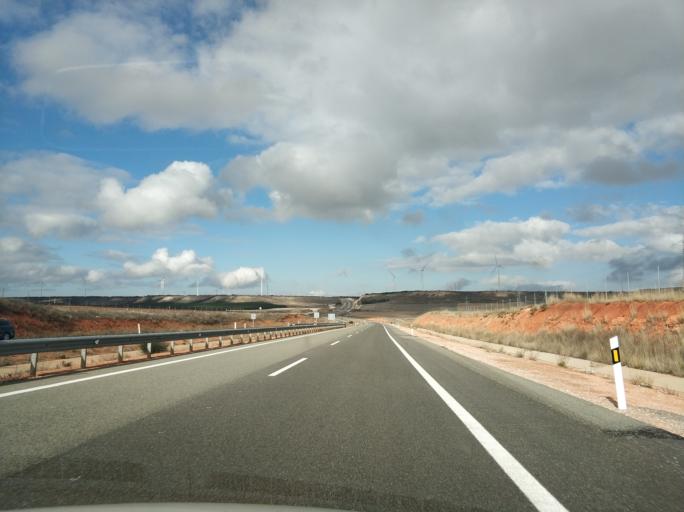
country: ES
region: Castille and Leon
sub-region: Provincia de Soria
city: Alcubilla de las Penas
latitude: 41.2725
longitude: -2.4743
